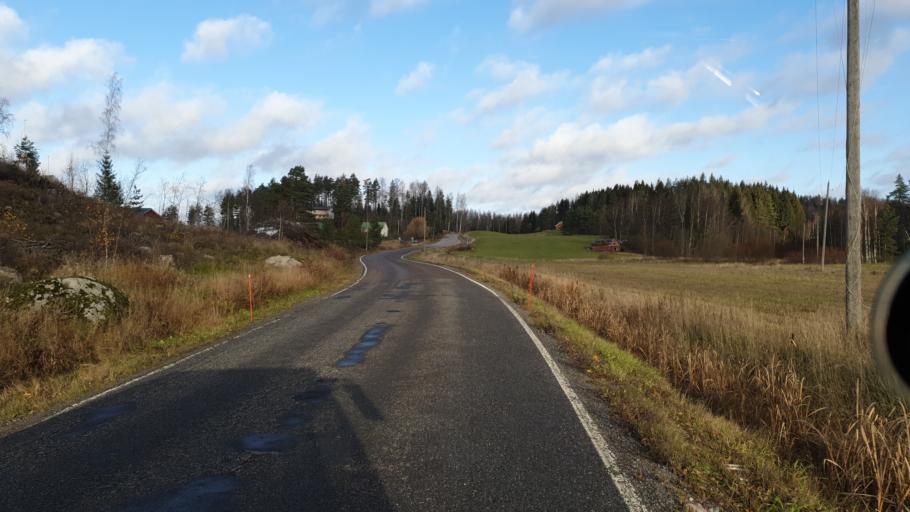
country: FI
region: Uusimaa
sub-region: Helsinki
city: Siuntio
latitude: 60.2664
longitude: 24.3043
